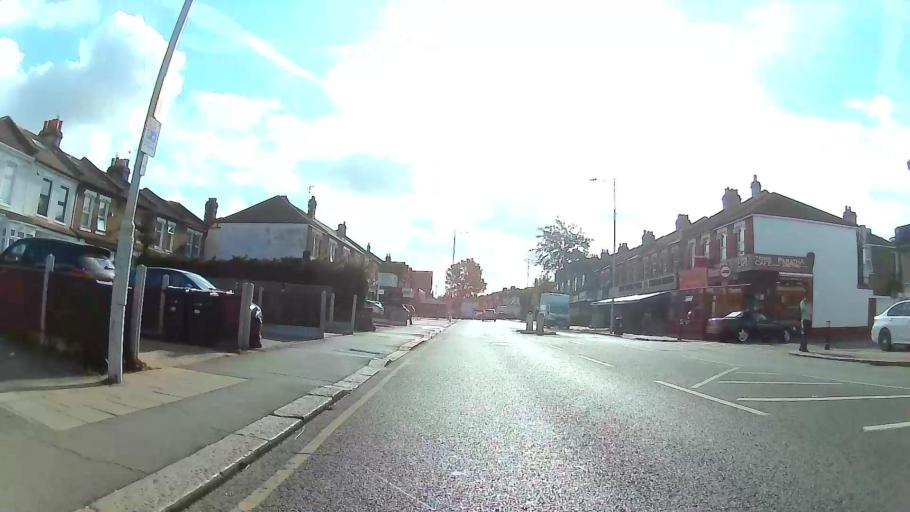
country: GB
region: England
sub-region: Greater London
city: Ilford
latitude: 51.5608
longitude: 0.0975
